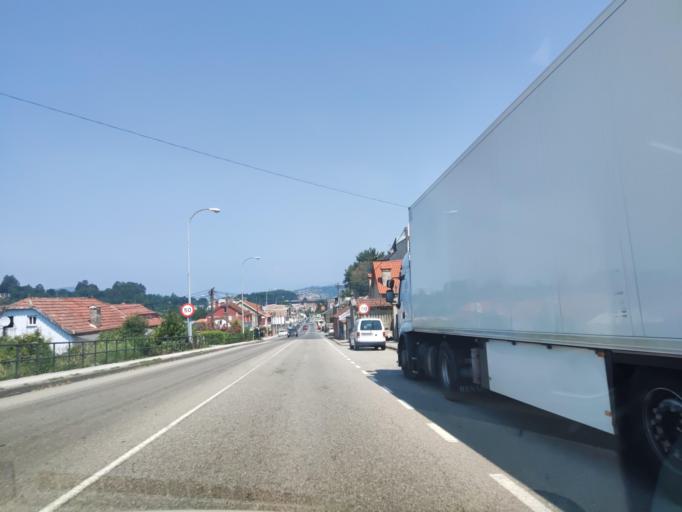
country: ES
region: Galicia
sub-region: Provincia de Pontevedra
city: Redondela
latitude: 42.2708
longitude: -8.6101
